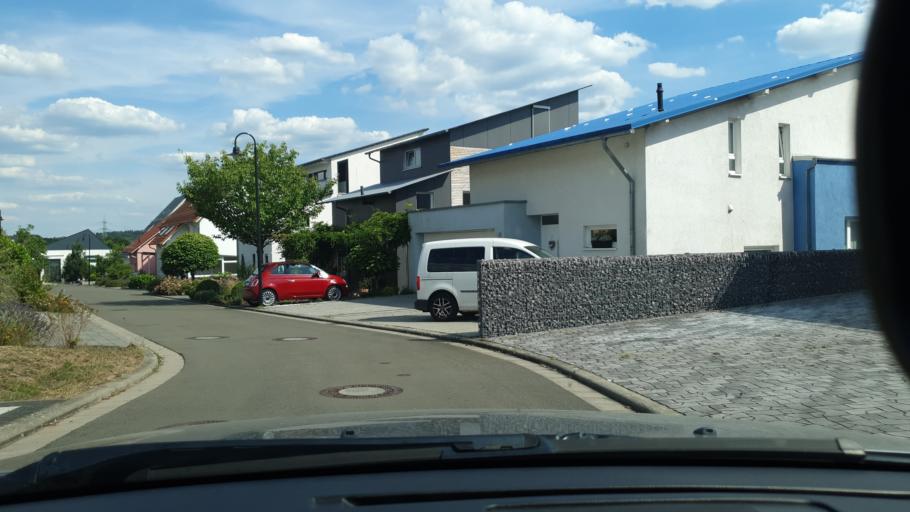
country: DE
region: Rheinland-Pfalz
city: Otterberg
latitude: 49.4970
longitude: 7.7604
